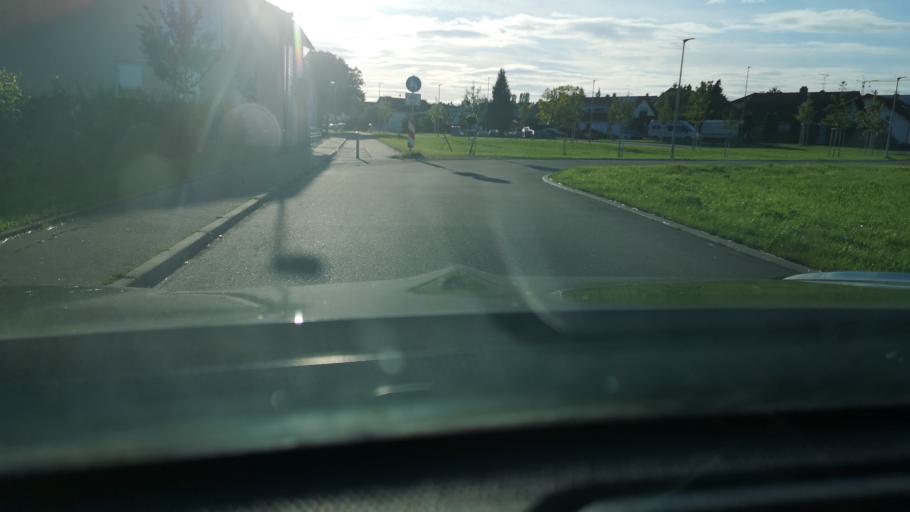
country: DE
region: Baden-Wuerttemberg
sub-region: Regierungsbezirk Stuttgart
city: Altenriet
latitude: 48.5901
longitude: 9.1852
